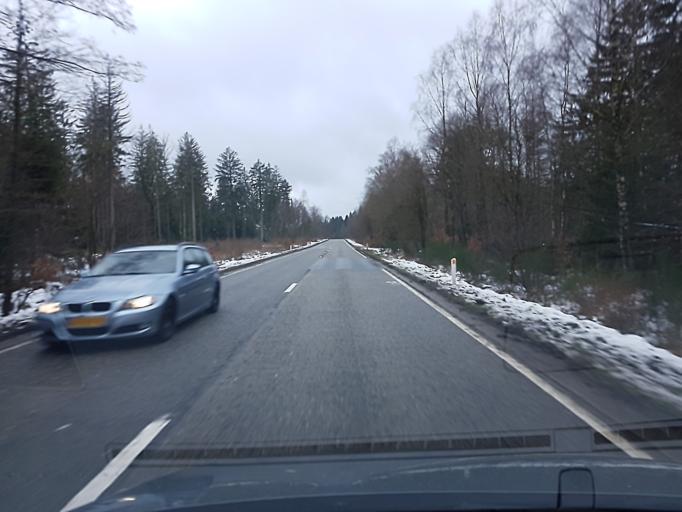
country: BE
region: Wallonia
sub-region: Province de Liege
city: Eupen
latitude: 50.5940
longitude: 6.0411
